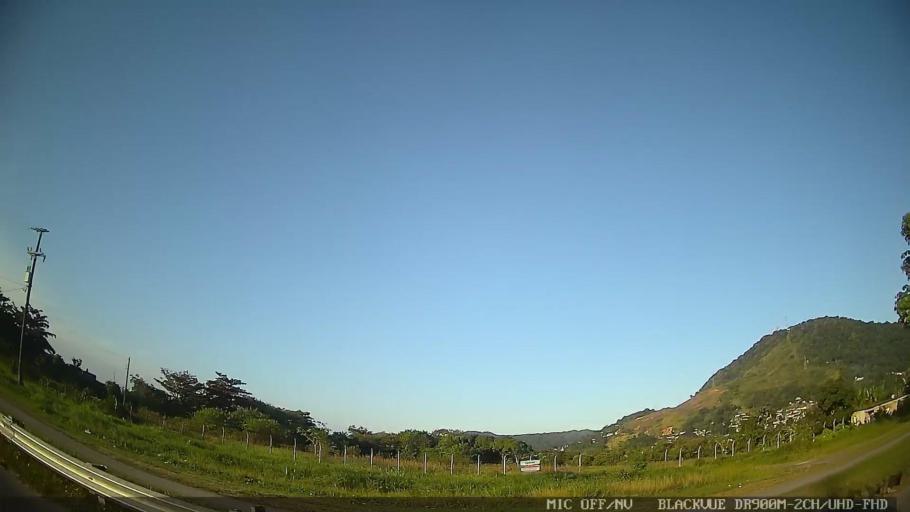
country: BR
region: Sao Paulo
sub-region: Guaruja
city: Guaruja
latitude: -23.9765
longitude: -46.2685
